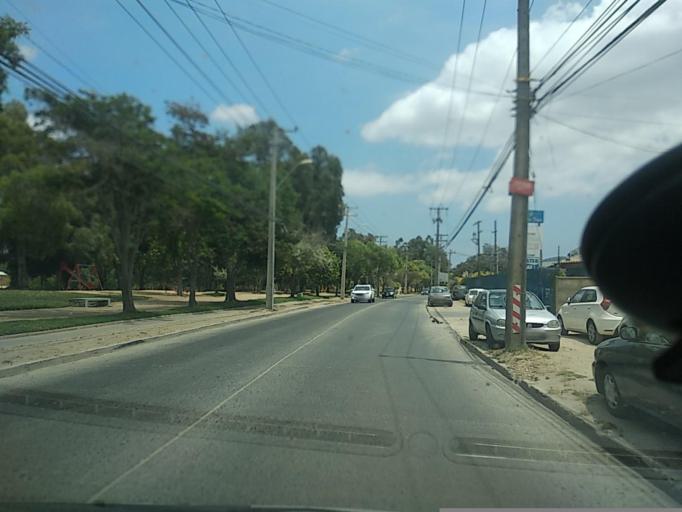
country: CL
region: Valparaiso
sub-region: Provincia de Marga Marga
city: Quilpue
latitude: -33.0410
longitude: -71.4147
